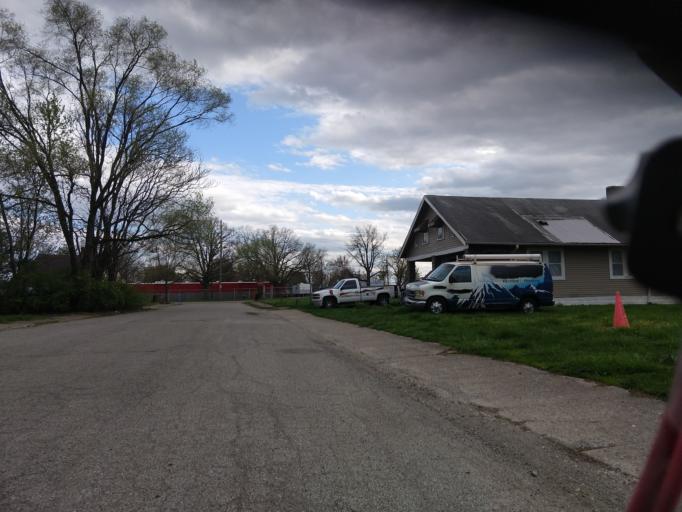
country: US
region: Indiana
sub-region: Marion County
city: Broad Ripple
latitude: 39.8336
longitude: -86.1301
